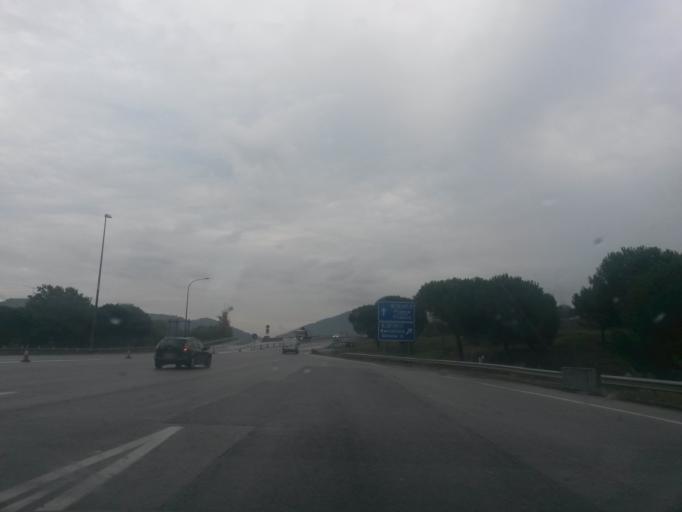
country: ES
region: Catalonia
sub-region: Provincia de Girona
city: Sarria de Ter
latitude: 42.0307
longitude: 2.8272
